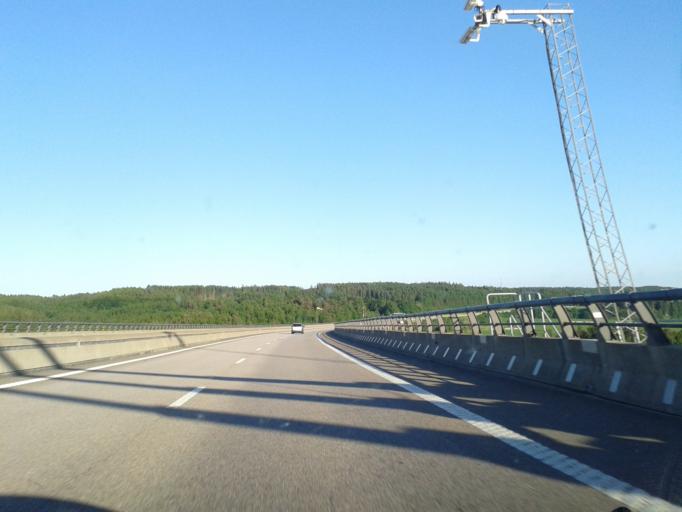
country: SE
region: Vaestra Goetaland
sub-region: Uddevalla Kommun
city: Uddevalla
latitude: 58.3232
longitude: 11.8488
